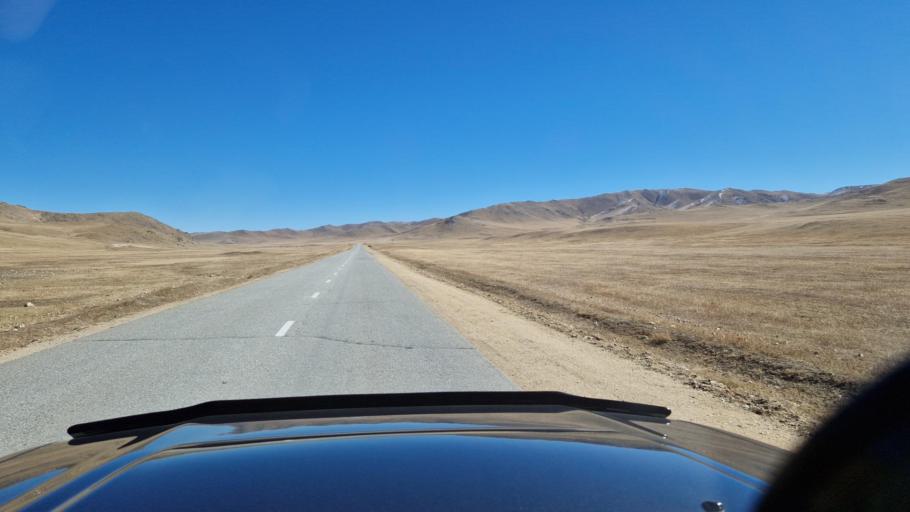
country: MN
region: Central Aimak
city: Bayandelger
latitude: 47.6936
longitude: 108.5084
